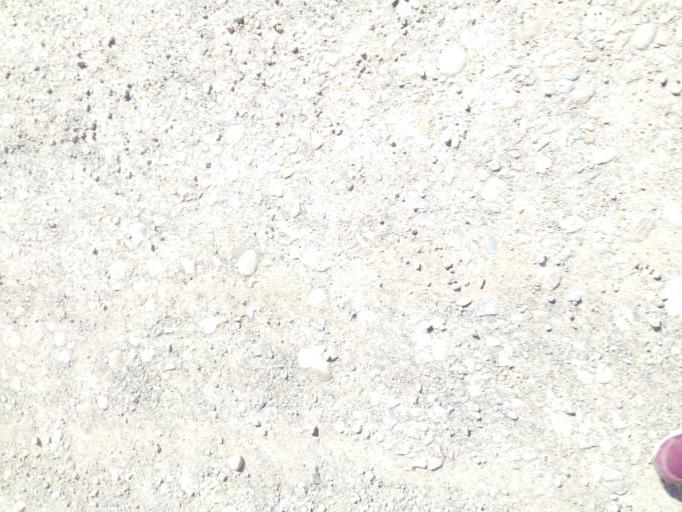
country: CO
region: Boyaca
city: Aquitania
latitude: 5.4655
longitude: -72.9232
